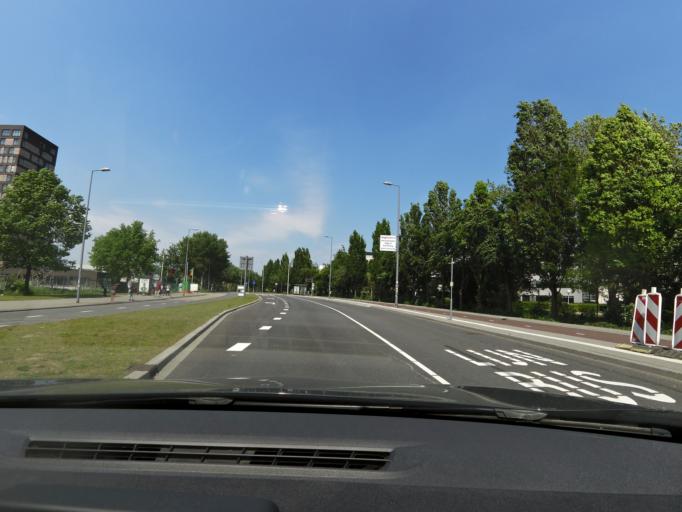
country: NL
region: South Holland
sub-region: Gemeente Rotterdam
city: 's-Gravenland
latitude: 51.9157
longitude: 4.5290
